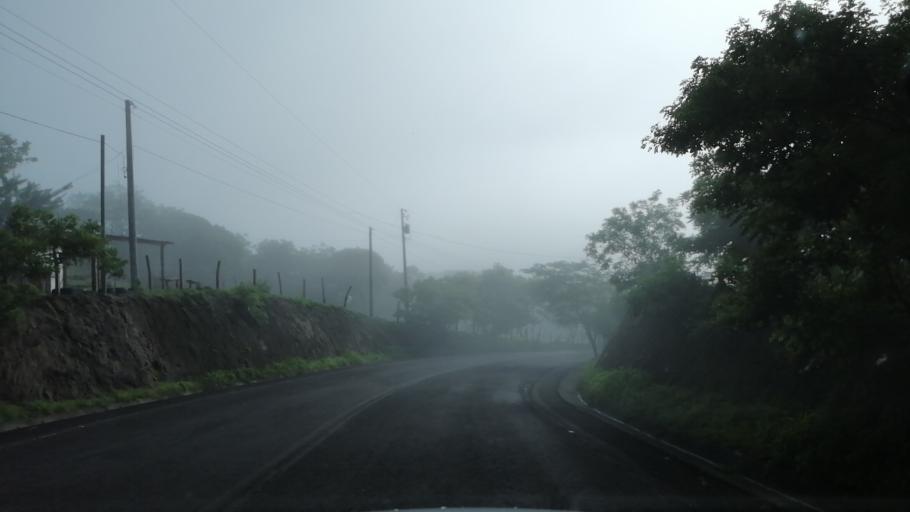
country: SV
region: Morazan
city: Cacaopera
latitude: 13.7882
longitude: -88.1158
